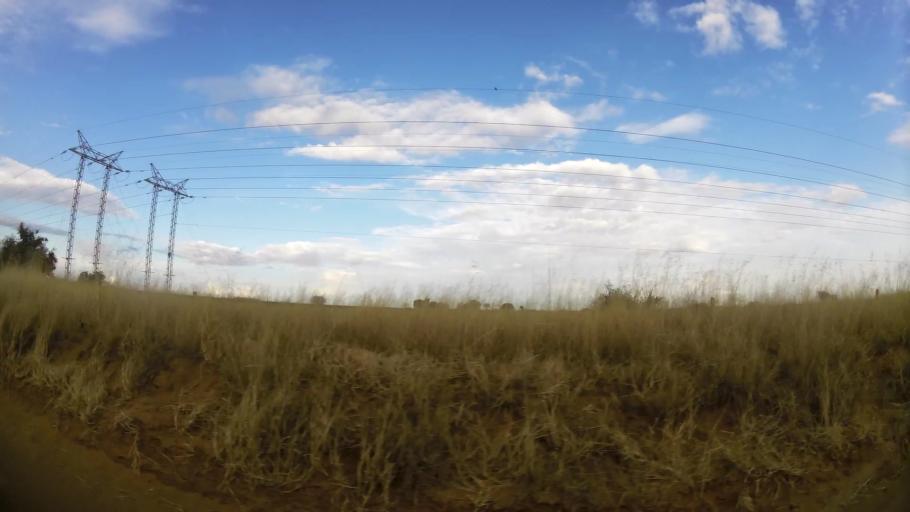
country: ZA
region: Orange Free State
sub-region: Lejweleputswa District Municipality
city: Welkom
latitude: -28.0131
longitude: 26.7238
